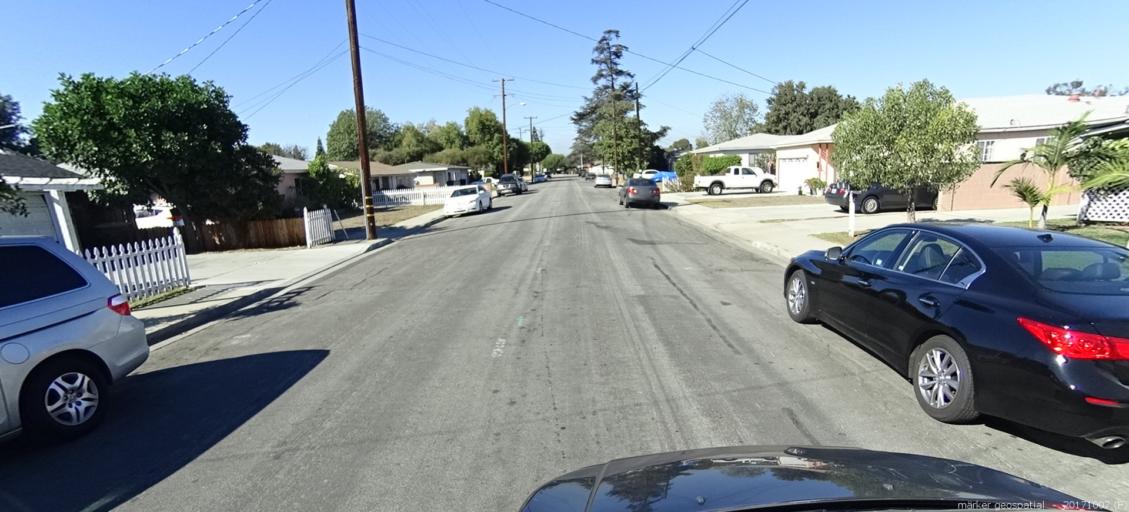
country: US
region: California
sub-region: Orange County
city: Stanton
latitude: 33.7761
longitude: -117.9741
